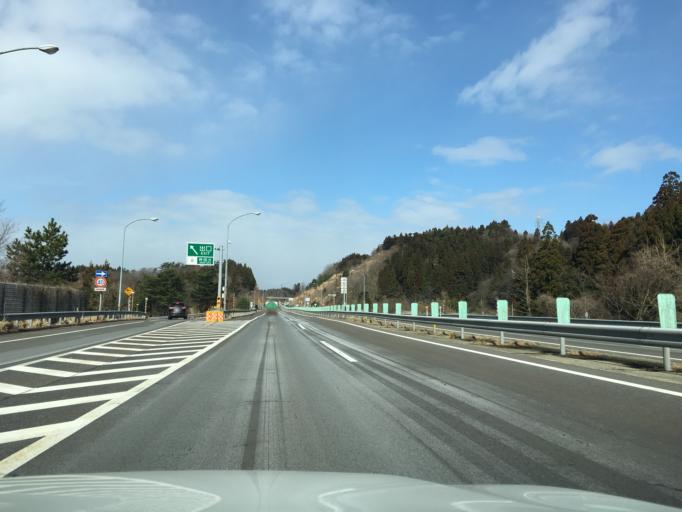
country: JP
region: Akita
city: Akita Shi
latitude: 39.7803
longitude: 140.1144
